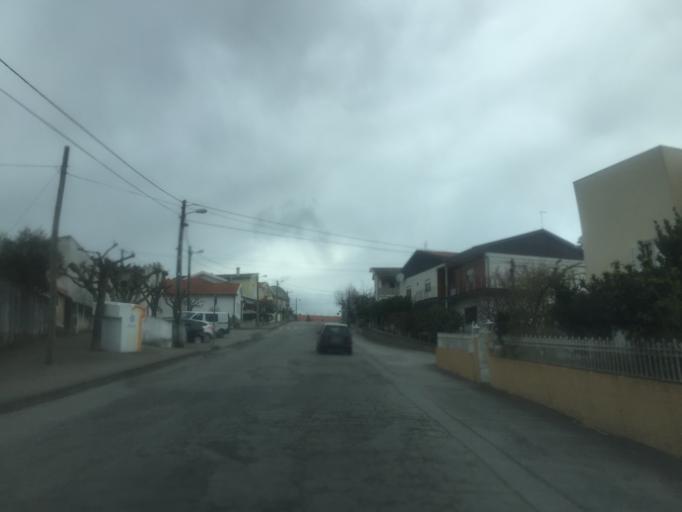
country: PT
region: Guarda
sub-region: Seia
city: Seia
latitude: 40.4023
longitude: -7.7146
